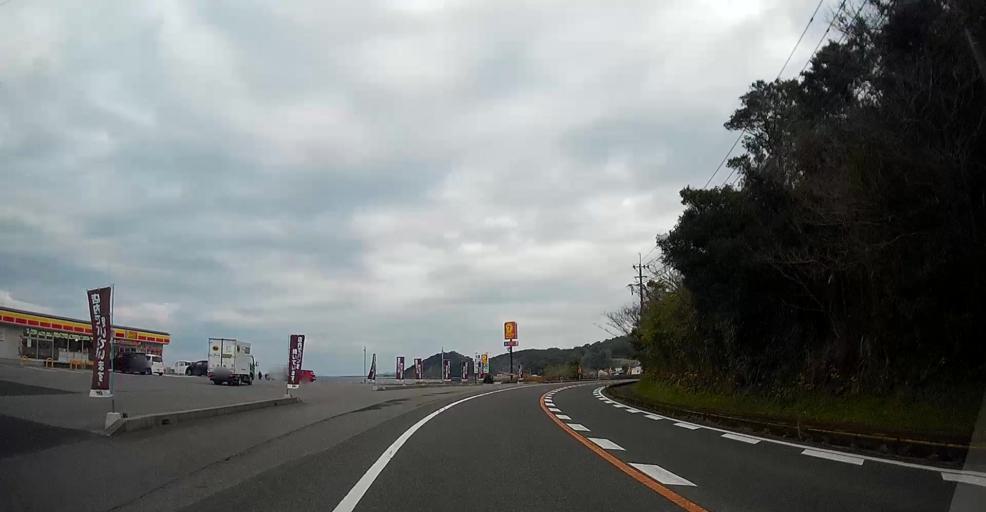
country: JP
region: Kumamoto
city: Hondo
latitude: 32.4608
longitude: 130.2310
